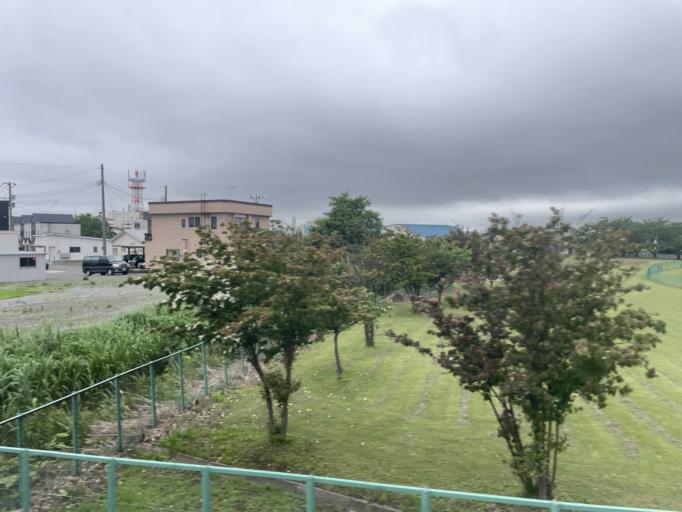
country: JP
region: Aomori
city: Goshogawara
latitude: 40.8168
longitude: 140.4434
